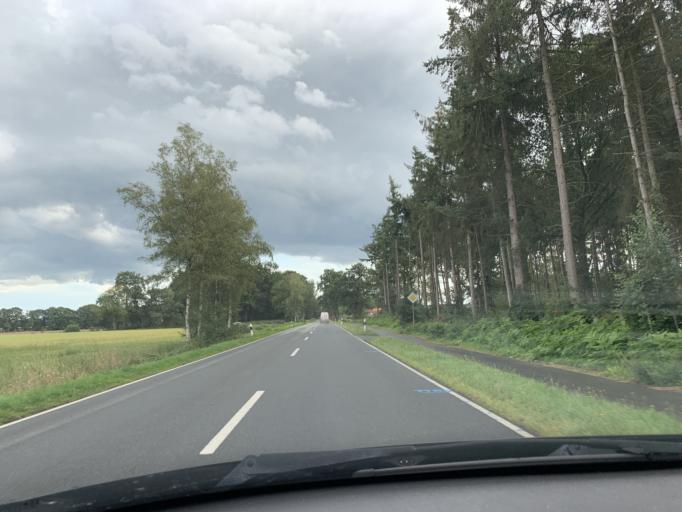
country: DE
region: Lower Saxony
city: Westerstede
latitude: 53.2999
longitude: 7.9165
